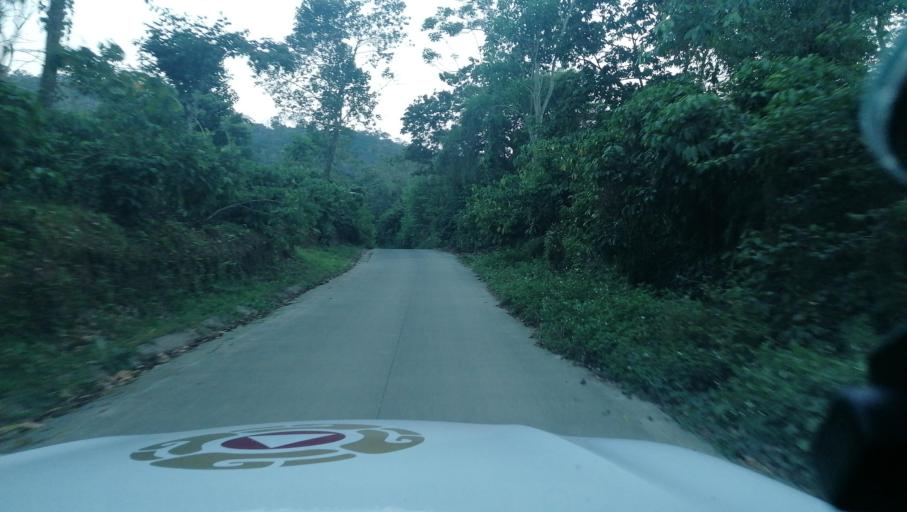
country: MX
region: Chiapas
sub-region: Cacahoatan
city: Benito Juarez
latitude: 15.0550
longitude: -92.2433
